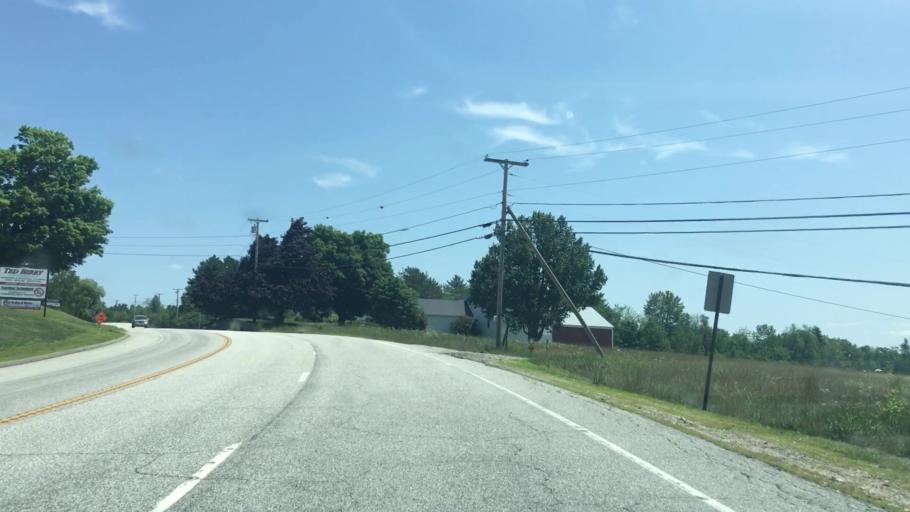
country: US
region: Maine
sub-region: Androscoggin County
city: Livermore Falls
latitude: 44.4426
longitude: -70.2109
